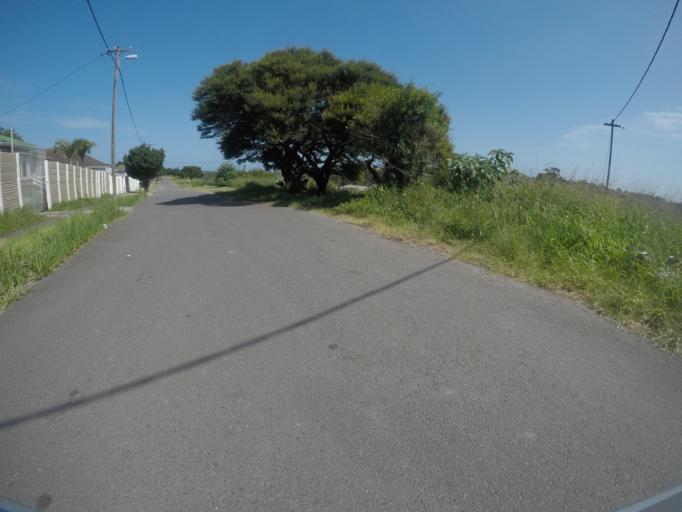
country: ZA
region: Eastern Cape
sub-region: Buffalo City Metropolitan Municipality
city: East London
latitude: -32.9778
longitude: 27.8682
